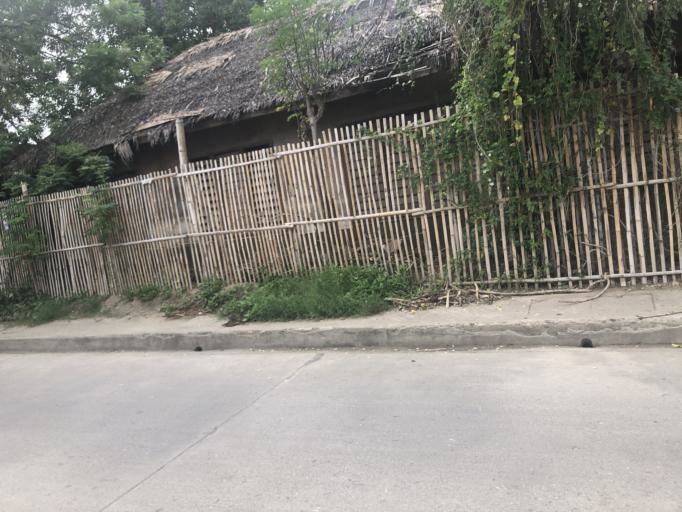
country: PH
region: Central Visayas
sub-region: Province of Negros Oriental
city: Dumaguete
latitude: 9.3037
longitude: 123.2997
